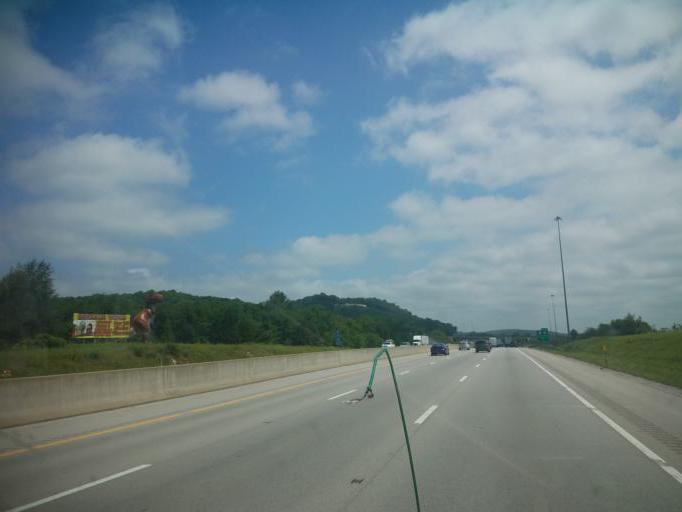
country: US
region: Kentucky
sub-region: Barren County
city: Cave City
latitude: 37.1315
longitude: -85.9825
